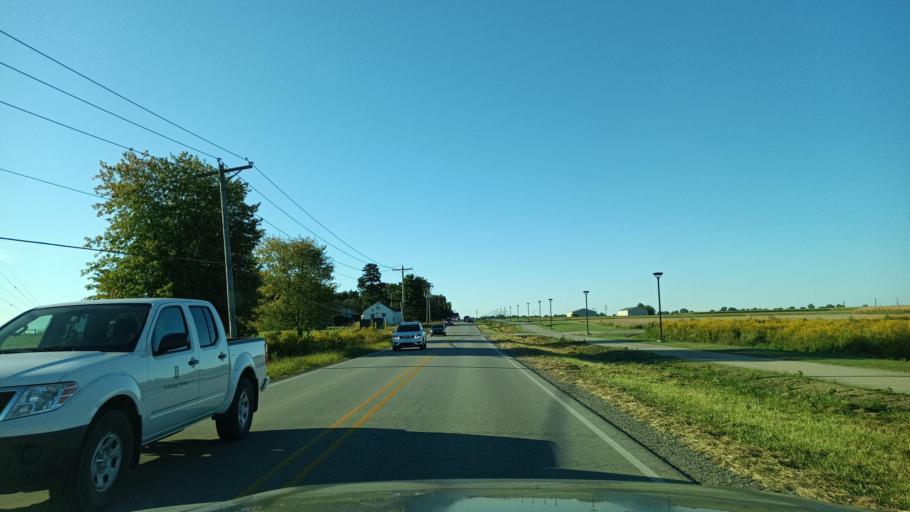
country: US
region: Illinois
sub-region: Champaign County
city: Savoy
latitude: 40.0815
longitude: -88.2385
